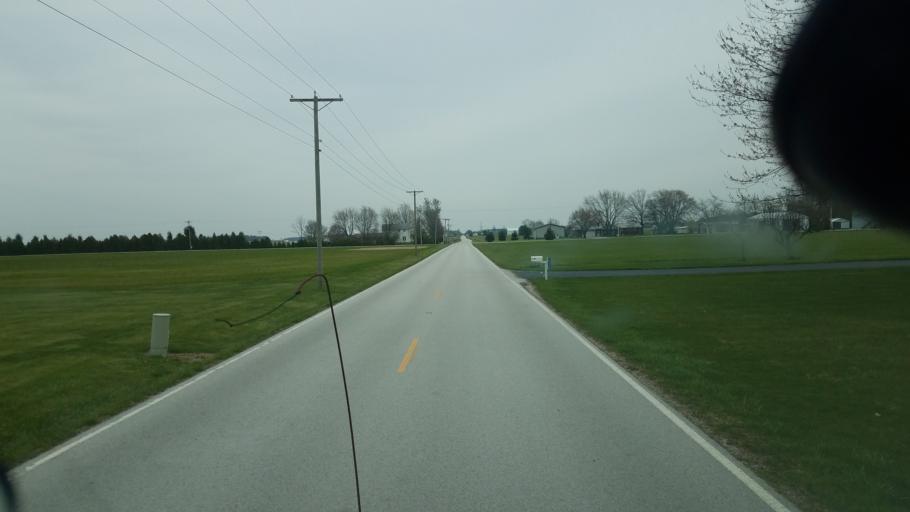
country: US
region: Ohio
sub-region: Wyandot County
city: Carey
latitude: 41.0505
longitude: -83.3659
